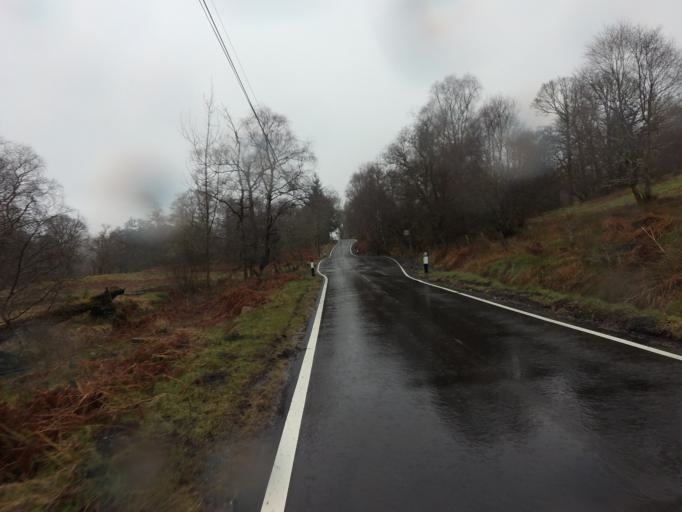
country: GB
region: Scotland
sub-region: West Dunbartonshire
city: Balloch
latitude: 56.1956
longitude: -4.5184
